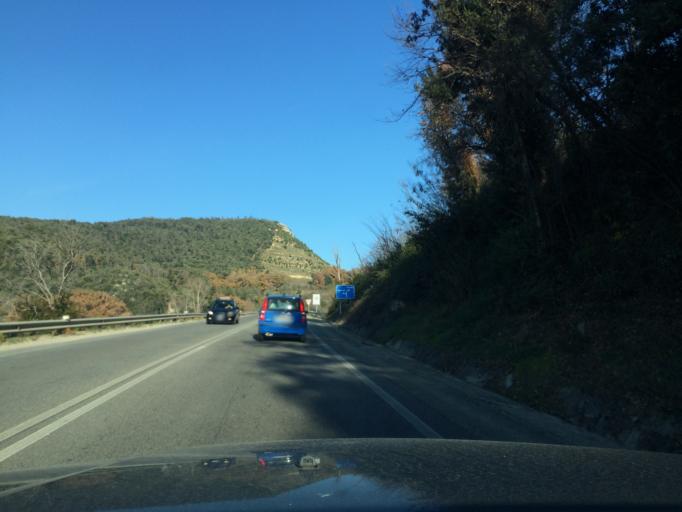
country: IT
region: Umbria
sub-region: Provincia di Terni
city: Fornole
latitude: 42.5365
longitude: 12.4763
